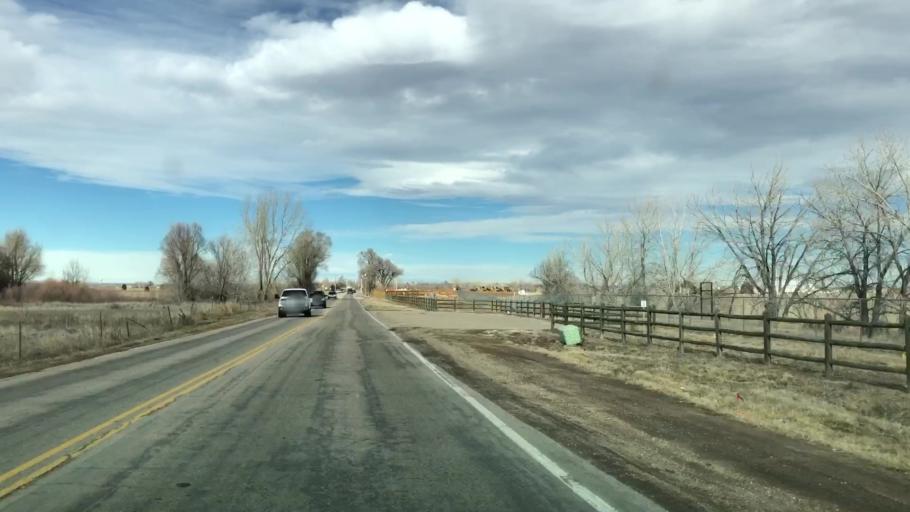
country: US
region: Colorado
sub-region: Weld County
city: Windsor
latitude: 40.4739
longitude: -104.9441
